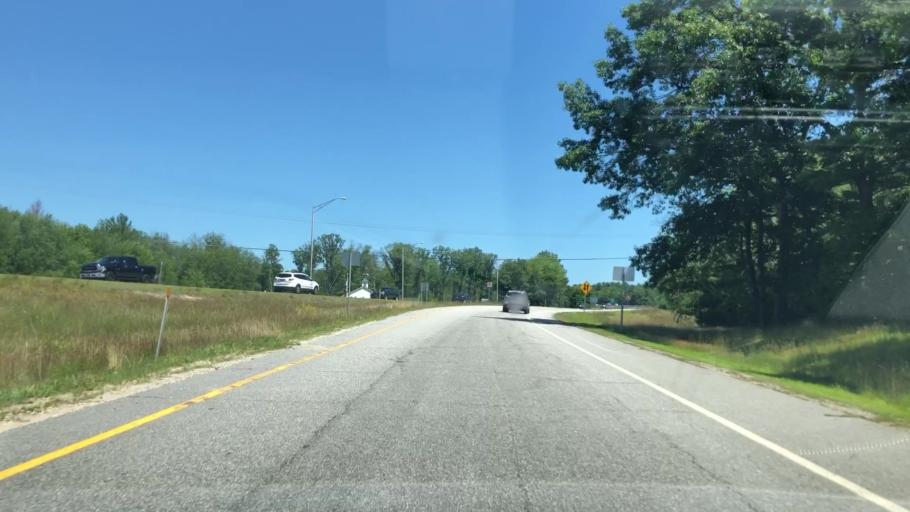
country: US
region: New Hampshire
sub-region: Hillsborough County
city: Milford
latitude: 42.8166
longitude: -71.6434
